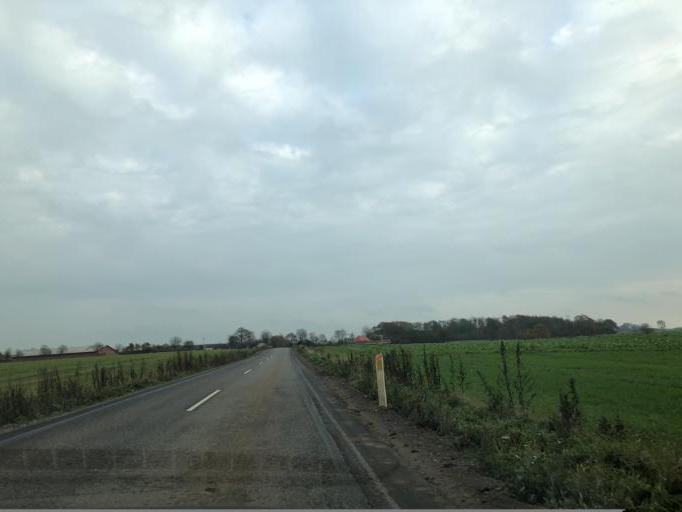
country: DK
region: Central Jutland
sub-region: Hedensted Kommune
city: Hornsyld
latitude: 55.7377
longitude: 9.7951
